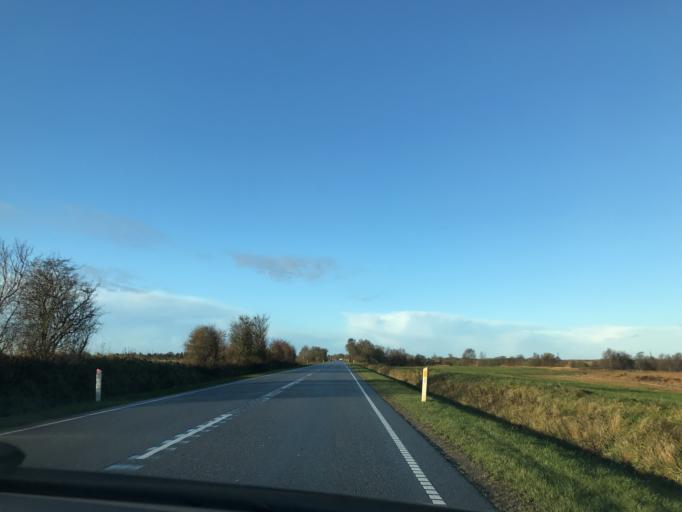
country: DK
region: South Denmark
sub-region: Haderslev Kommune
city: Vojens
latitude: 55.1727
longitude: 9.3398
